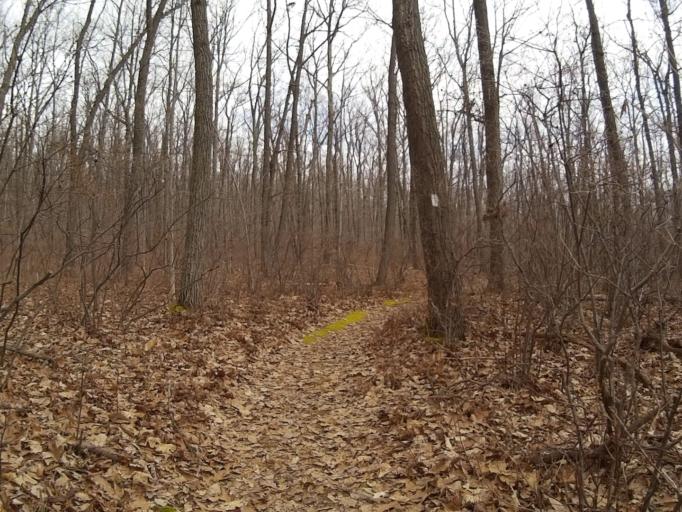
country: US
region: Pennsylvania
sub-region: Centre County
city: Lemont
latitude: 40.8097
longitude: -77.7971
